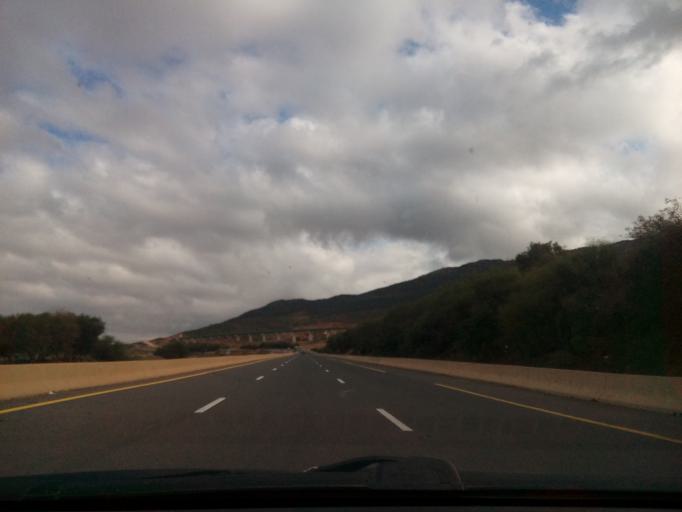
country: DZ
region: Tlemcen
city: Sidi Abdelli
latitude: 35.0095
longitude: -1.1706
